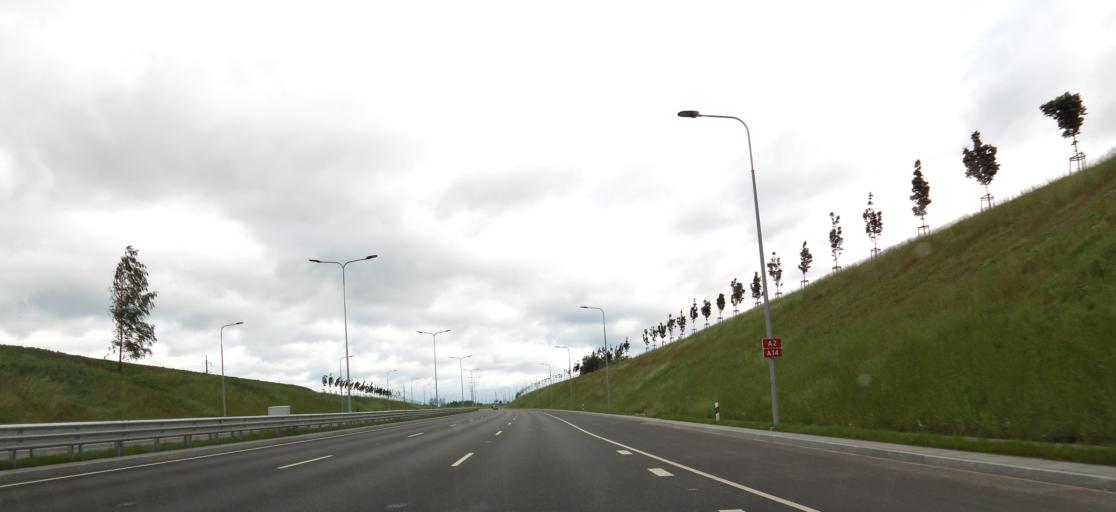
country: LT
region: Vilnius County
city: Justiniskes
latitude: 54.7085
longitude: 25.2099
